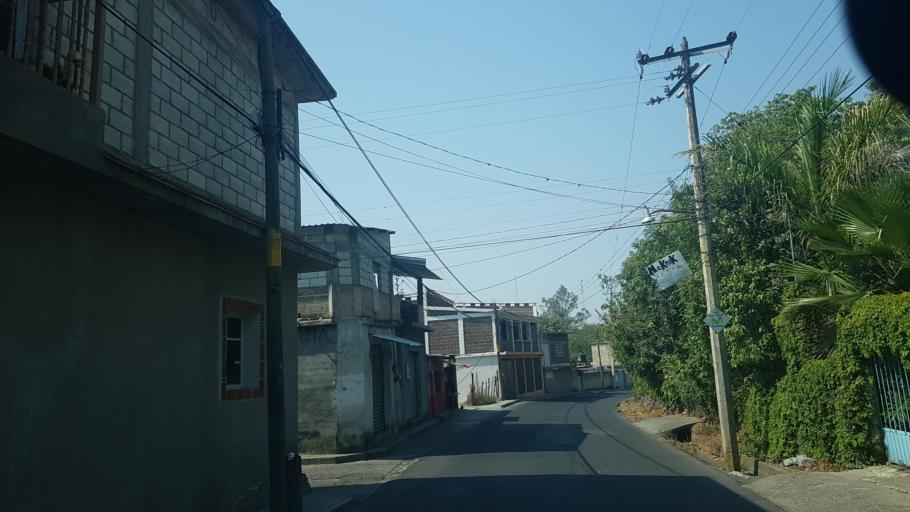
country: MX
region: Morelos
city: Tlacotepec
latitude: 18.8116
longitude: -98.7544
